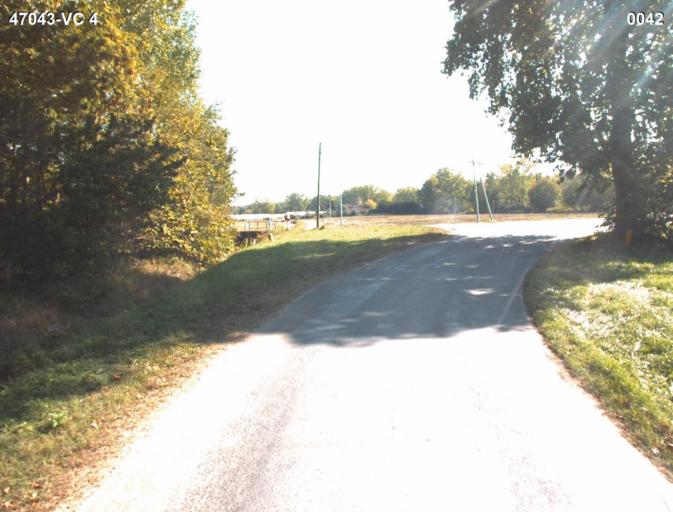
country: FR
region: Aquitaine
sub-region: Departement du Lot-et-Garonne
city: Buzet-sur-Baise
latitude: 44.2593
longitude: 0.3073
